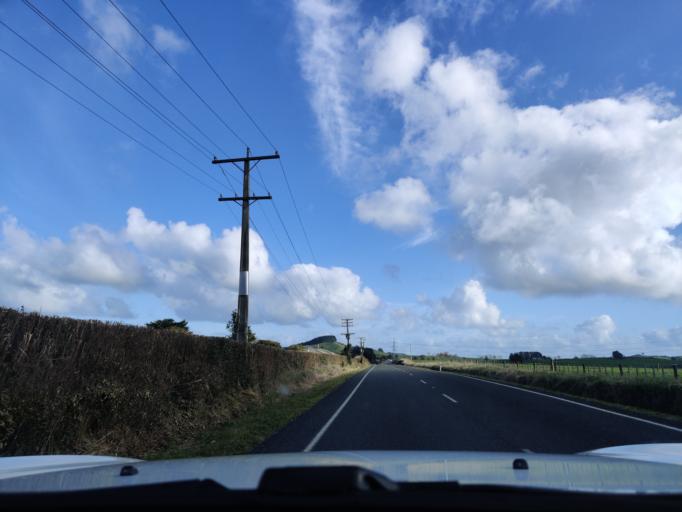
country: NZ
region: Waikato
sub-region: Waikato District
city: Te Kauwhata
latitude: -37.3609
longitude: 175.2538
